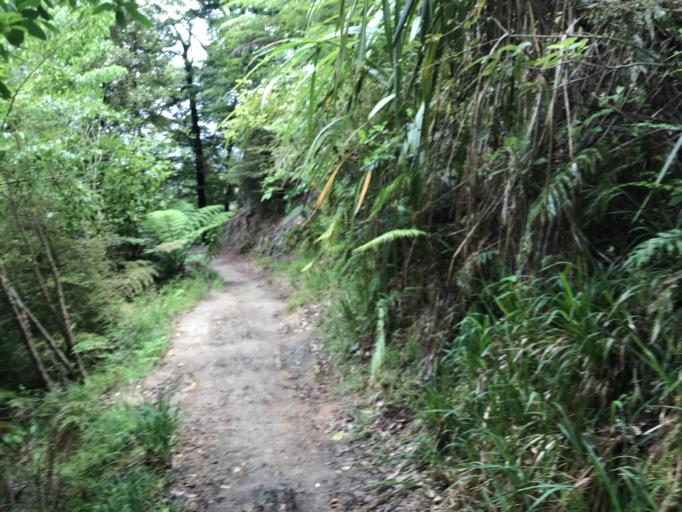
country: NZ
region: Marlborough
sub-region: Marlborough District
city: Picton
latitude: -41.2491
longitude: 173.9543
